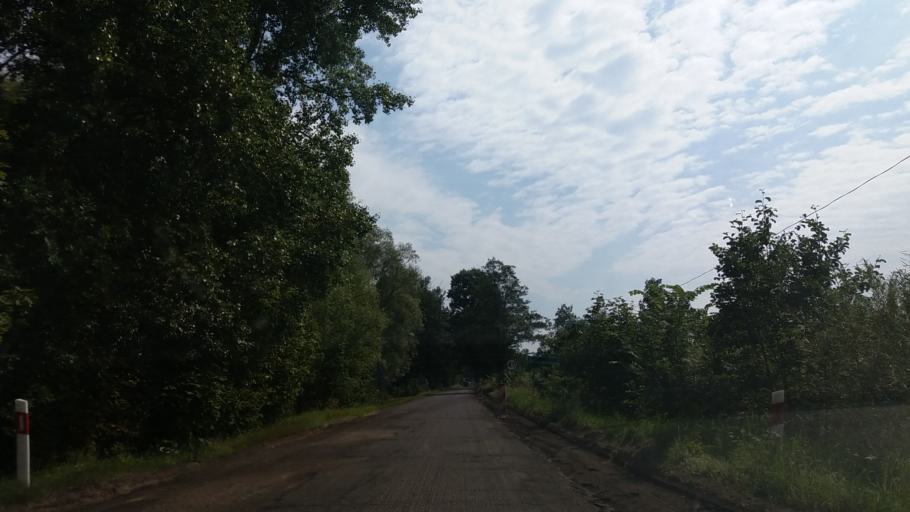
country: PL
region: Lubusz
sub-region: Powiat strzelecko-drezdenecki
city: Stare Kurowo
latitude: 52.7732
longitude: 15.6411
